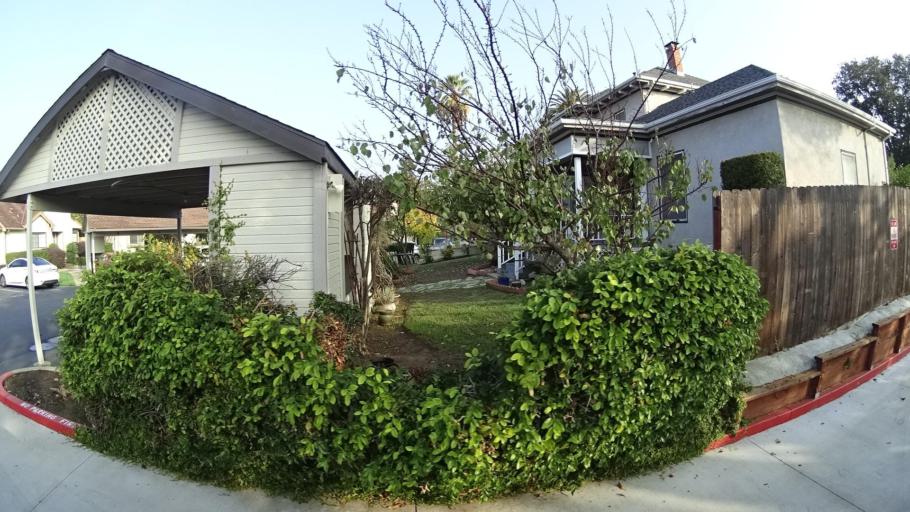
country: US
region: California
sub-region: Sacramento County
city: Elk Grove
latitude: 38.4066
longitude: -121.3680
